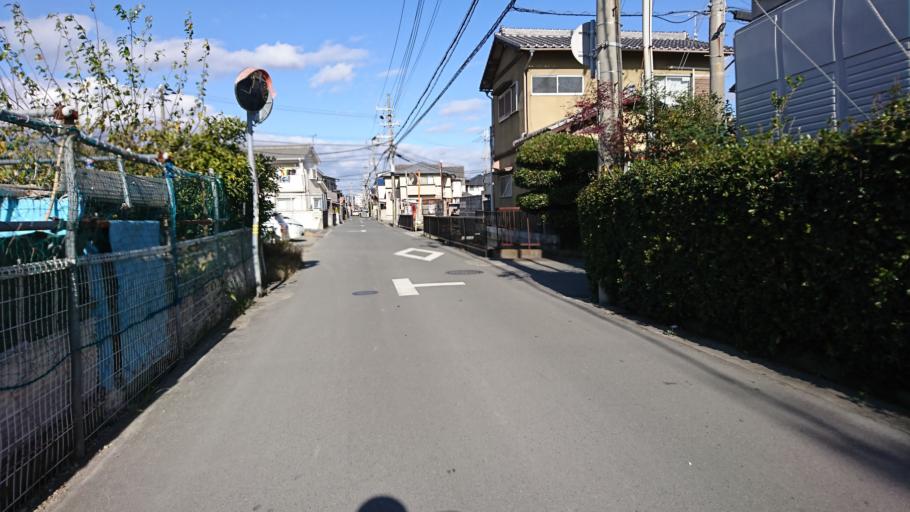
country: JP
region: Hyogo
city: Kakogawacho-honmachi
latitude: 34.7702
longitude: 134.7747
